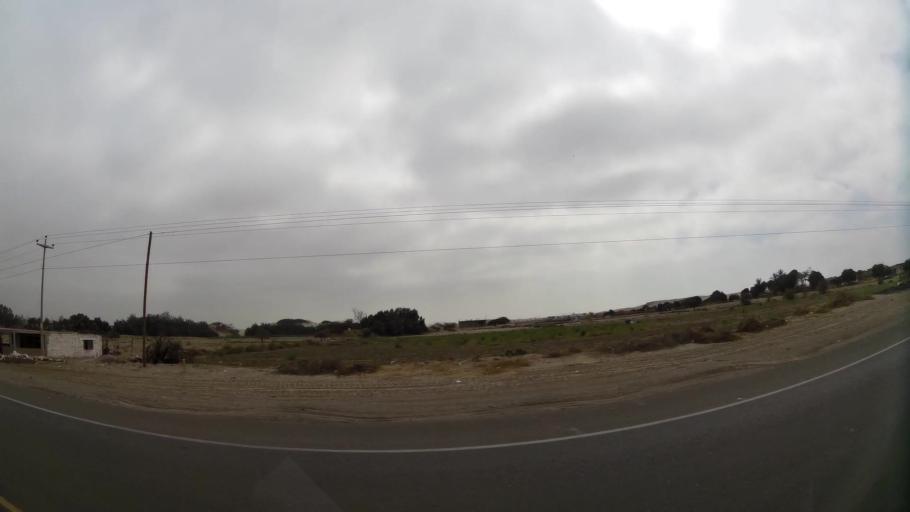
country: PE
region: Ica
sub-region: Provincia de Pisco
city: Independencia
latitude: -13.9088
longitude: -76.0220
